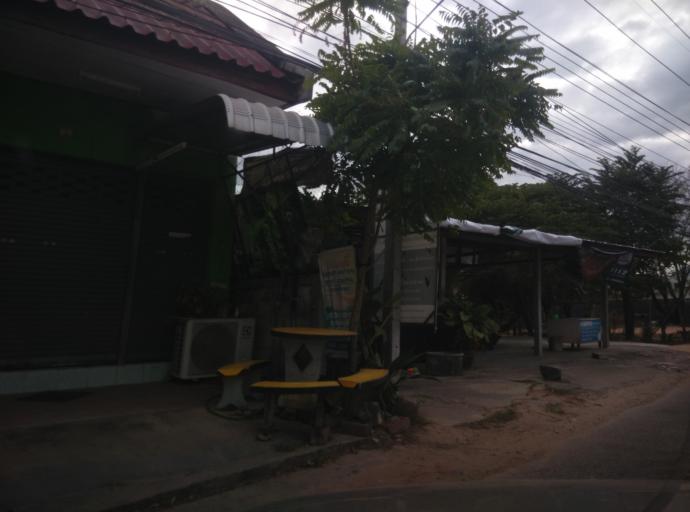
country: TH
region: Sisaket
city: Si Sa Ket
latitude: 15.1151
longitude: 104.3556
